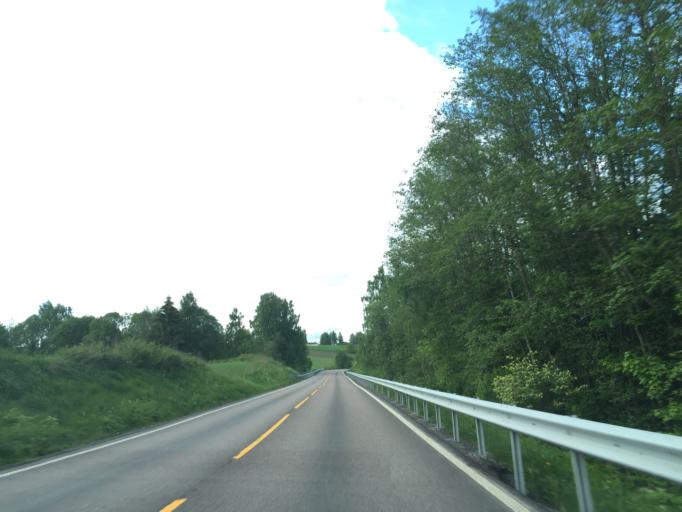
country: NO
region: Akershus
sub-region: Fet
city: Fetsund
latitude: 59.9403
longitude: 11.1907
